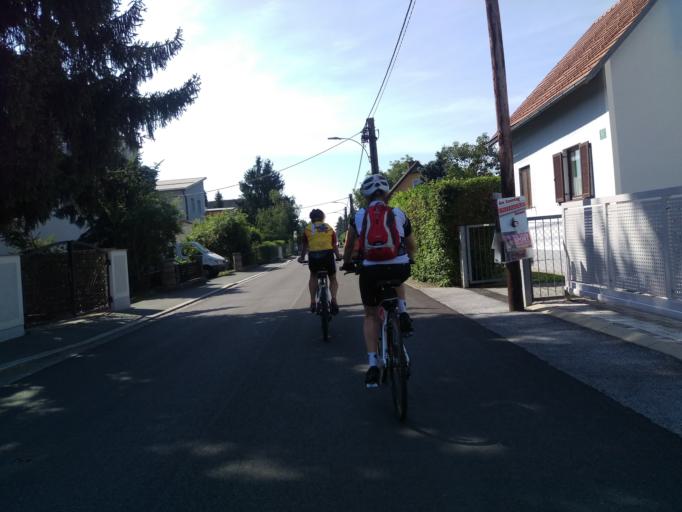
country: AT
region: Styria
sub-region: Politischer Bezirk Graz-Umgebung
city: Feldkirchen bei Graz
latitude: 47.0231
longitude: 15.4588
